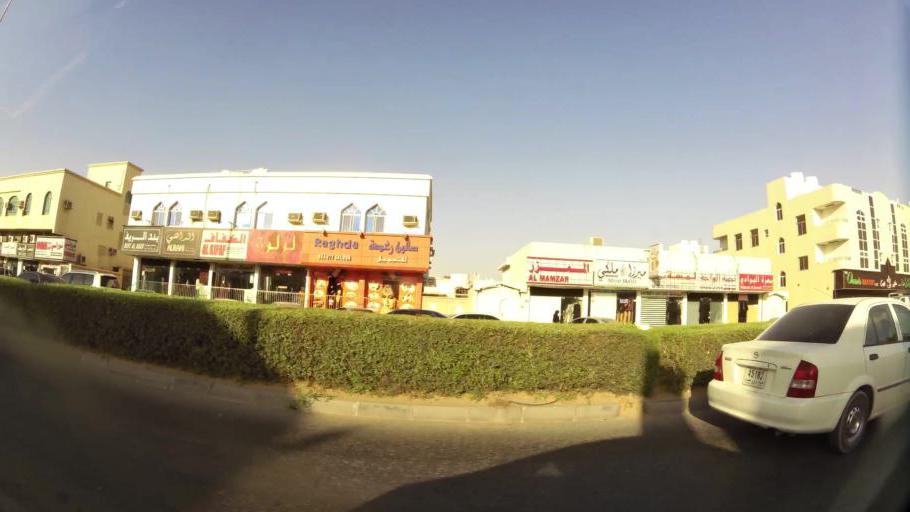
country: AE
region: Ajman
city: Ajman
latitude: 25.3950
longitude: 55.5050
